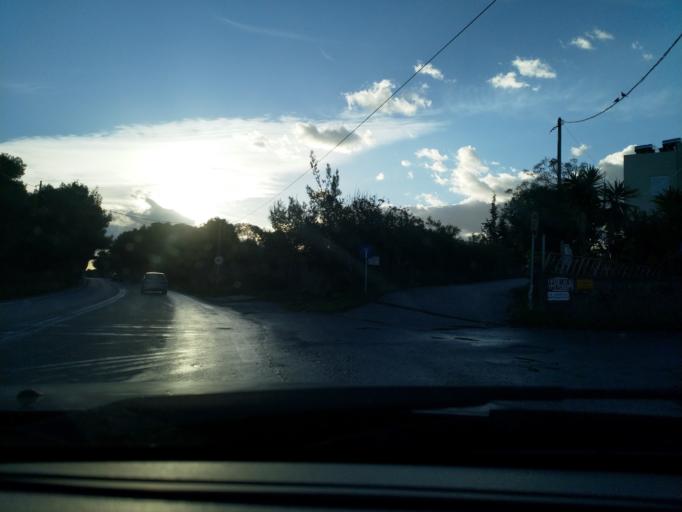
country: GR
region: Crete
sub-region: Nomos Chanias
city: Pithari
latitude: 35.5174
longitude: 24.0728
